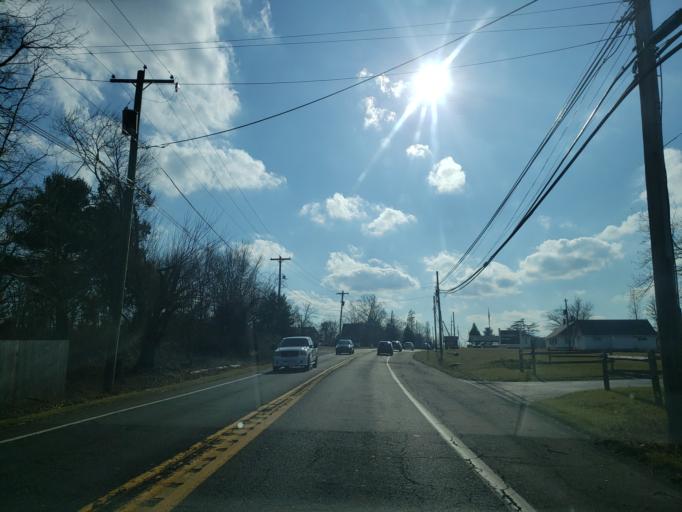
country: US
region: Pennsylvania
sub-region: Bucks County
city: Doylestown
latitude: 40.3344
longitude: -75.0494
